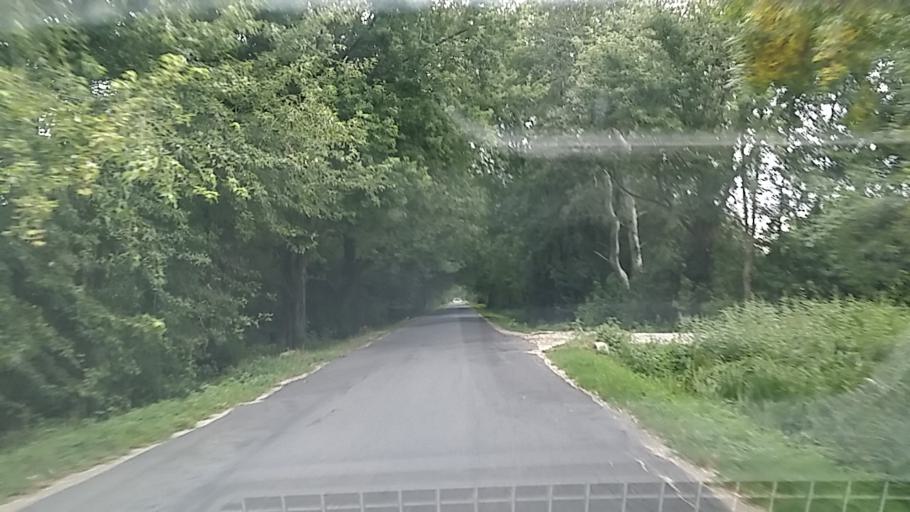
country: HU
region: Gyor-Moson-Sopron
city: Kapuvar
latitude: 47.6488
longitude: 17.1051
